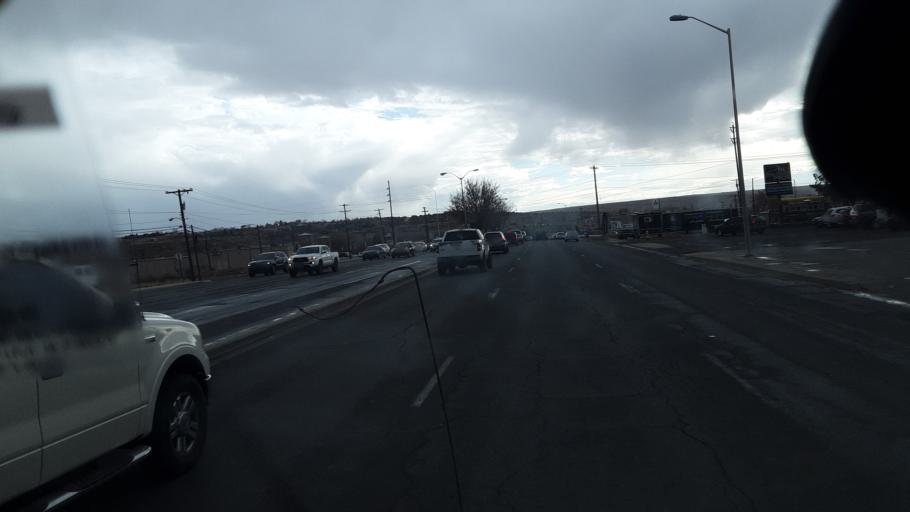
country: US
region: New Mexico
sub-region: San Juan County
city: Farmington
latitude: 36.7587
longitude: -108.1561
